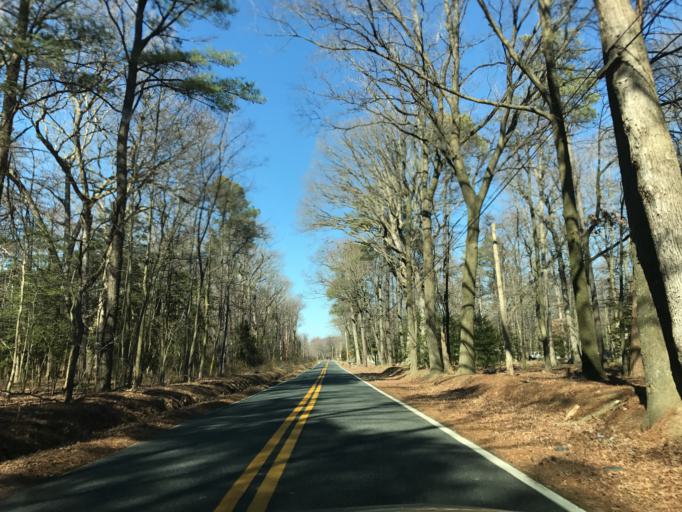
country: US
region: Maryland
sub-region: Queen Anne's County
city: Stevensville
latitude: 38.9342
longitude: -76.3537
